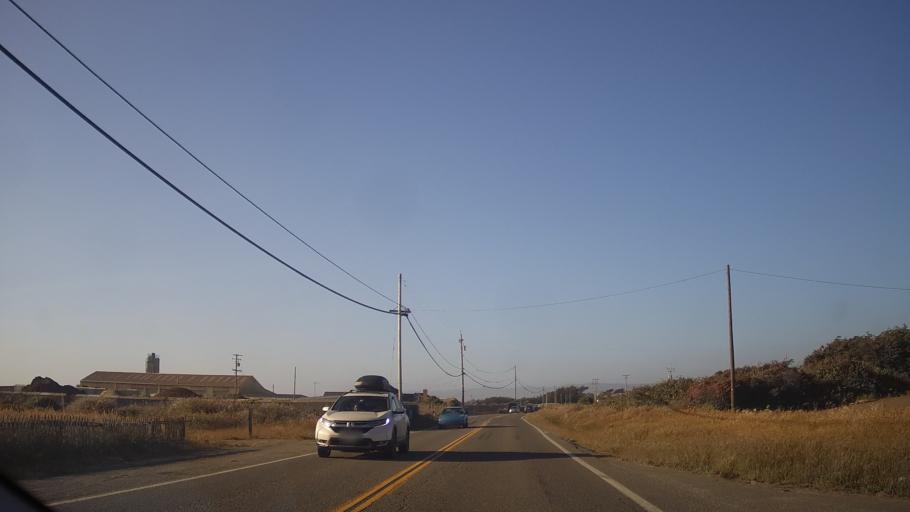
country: US
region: California
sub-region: Mendocino County
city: Fort Bragg
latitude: 39.4641
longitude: -123.8055
